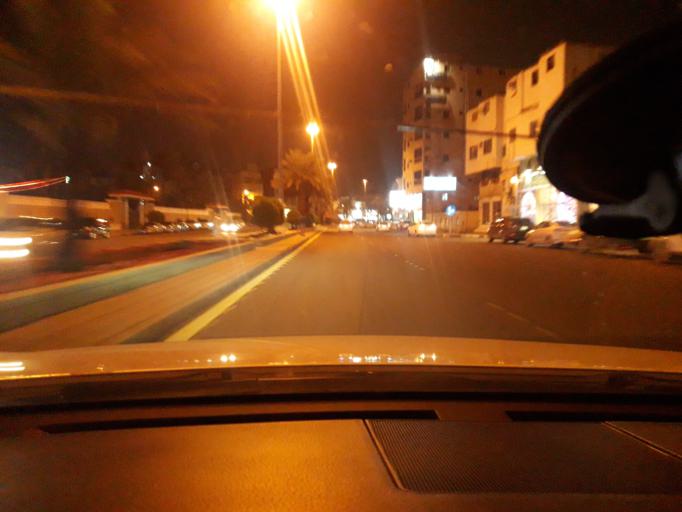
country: SA
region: Al Madinah al Munawwarah
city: Sultanah
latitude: 24.4817
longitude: 39.5995
